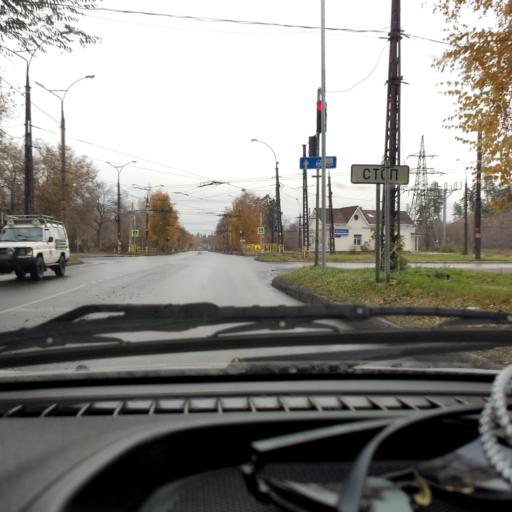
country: RU
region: Samara
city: Tol'yatti
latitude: 53.5059
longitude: 49.3908
